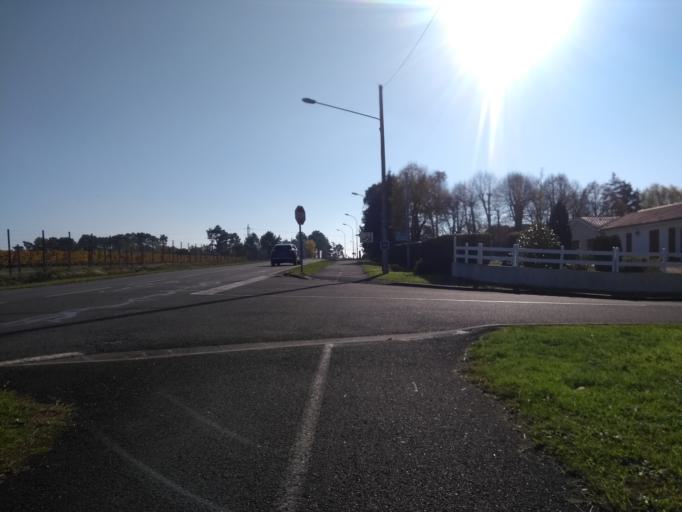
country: FR
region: Aquitaine
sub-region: Departement de la Gironde
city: Leognan
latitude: 44.7441
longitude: -0.6184
